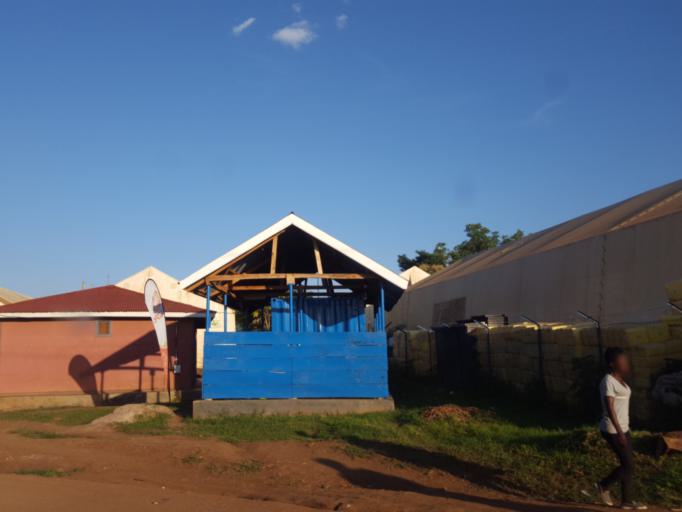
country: UG
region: Western Region
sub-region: Kibale District
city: Kagadi
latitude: 1.1896
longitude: 30.7815
